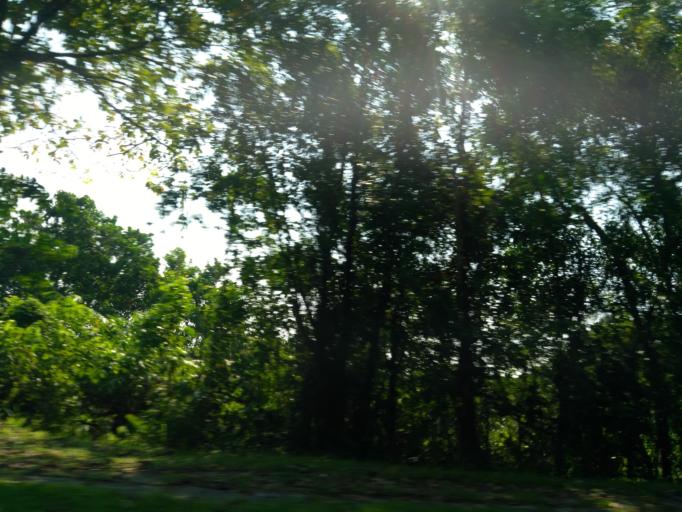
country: MY
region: Sarawak
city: Kuching
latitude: 1.7313
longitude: 110.3148
